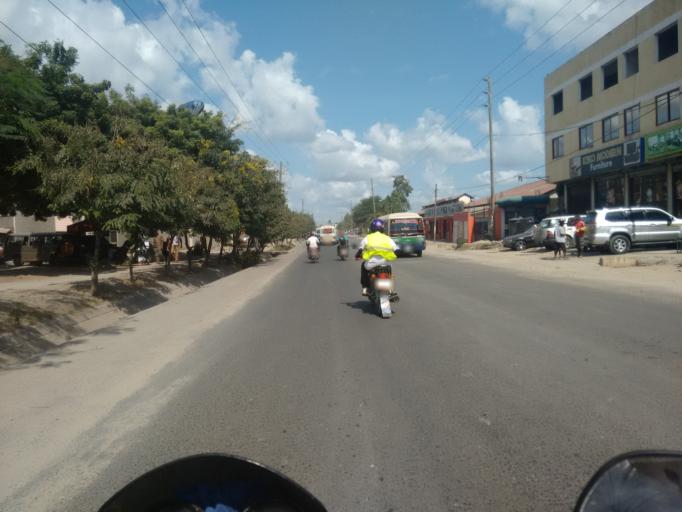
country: TZ
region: Dar es Salaam
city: Dar es Salaam
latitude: -6.8360
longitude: 39.2708
